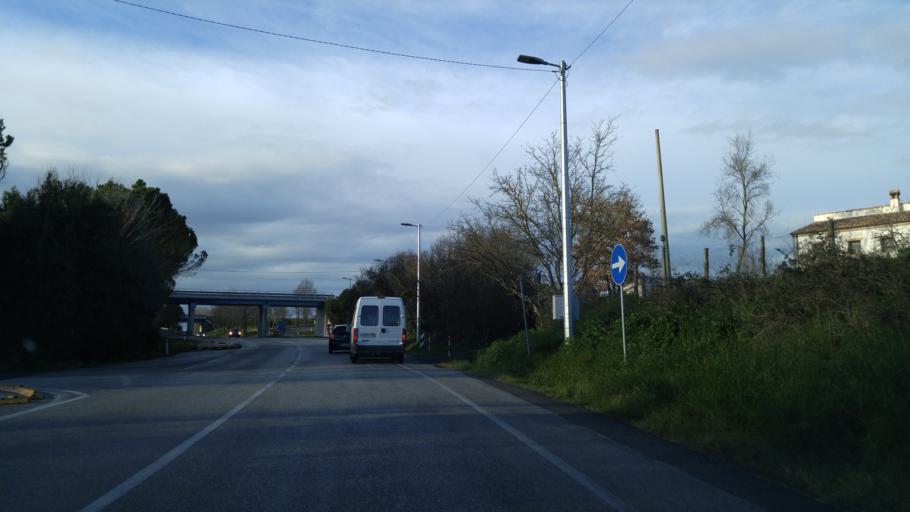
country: IT
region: The Marches
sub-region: Provincia di Ancona
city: Camerano
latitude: 43.5200
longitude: 13.5364
